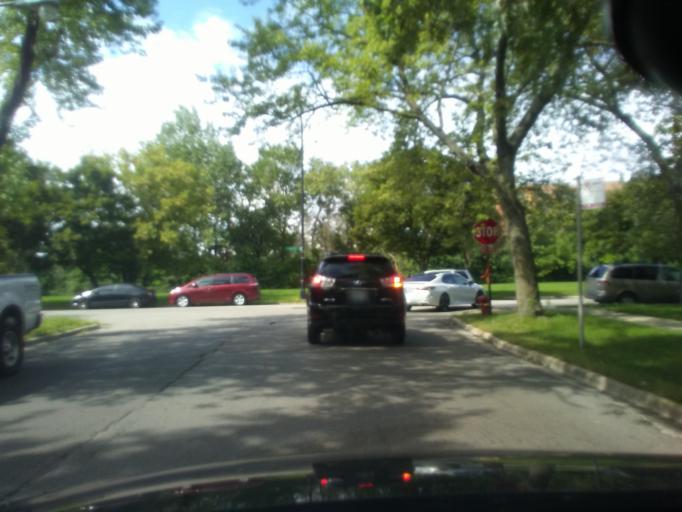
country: US
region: Illinois
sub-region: Cook County
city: Lincolnwood
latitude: 41.9939
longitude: -87.7089
